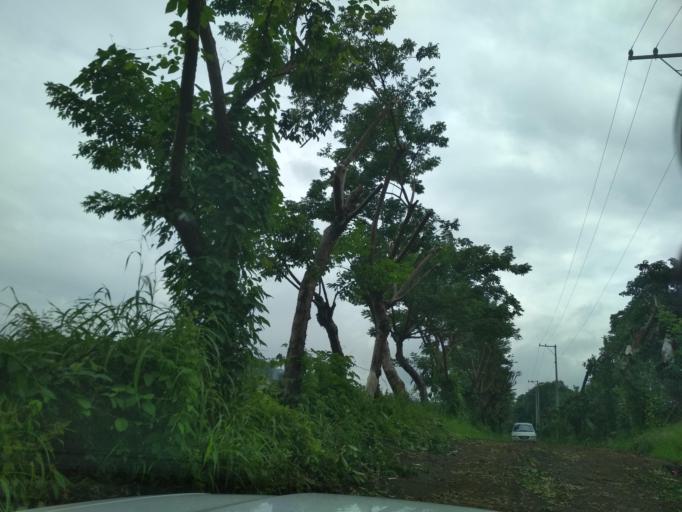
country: MX
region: Veracruz
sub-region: San Andres Tuxtla
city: Matacapan
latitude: 18.4347
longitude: -95.1519
